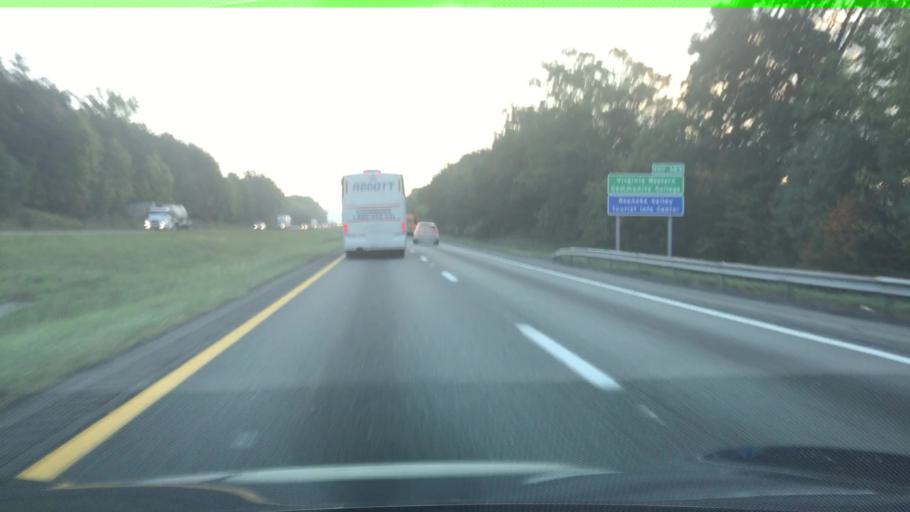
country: US
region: Virginia
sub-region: City of Salem
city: Salem
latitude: 37.3356
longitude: -80.0137
